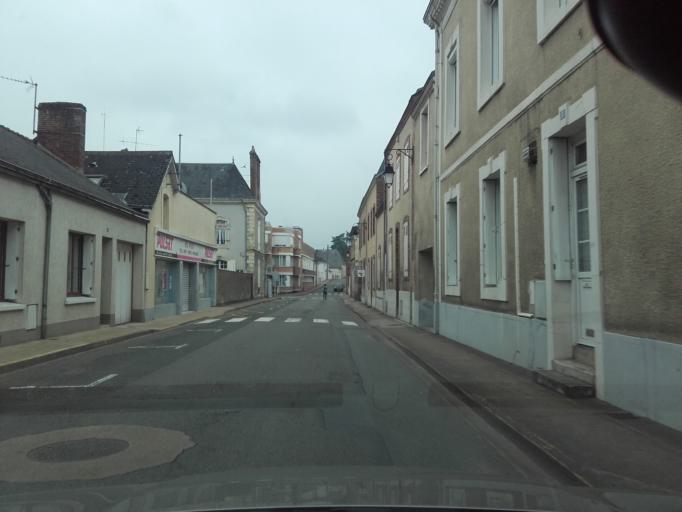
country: FR
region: Pays de la Loire
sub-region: Departement de la Sarthe
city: Saint-Calais
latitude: 47.9201
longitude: 0.7422
